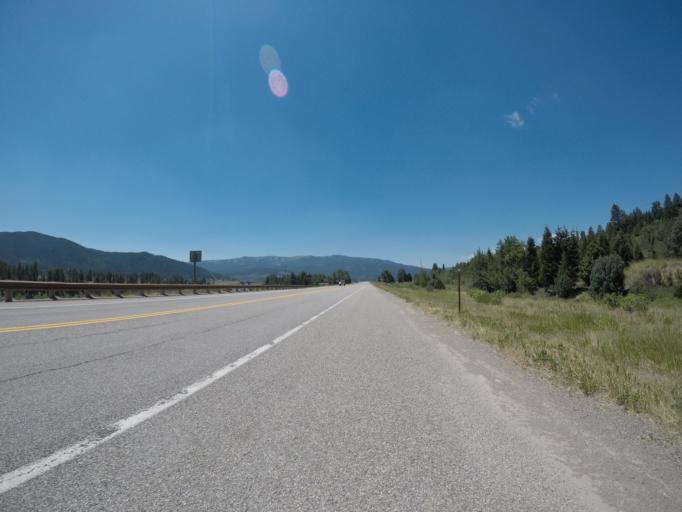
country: US
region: Wyoming
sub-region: Teton County
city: Hoback
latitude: 43.1754
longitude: -111.0032
